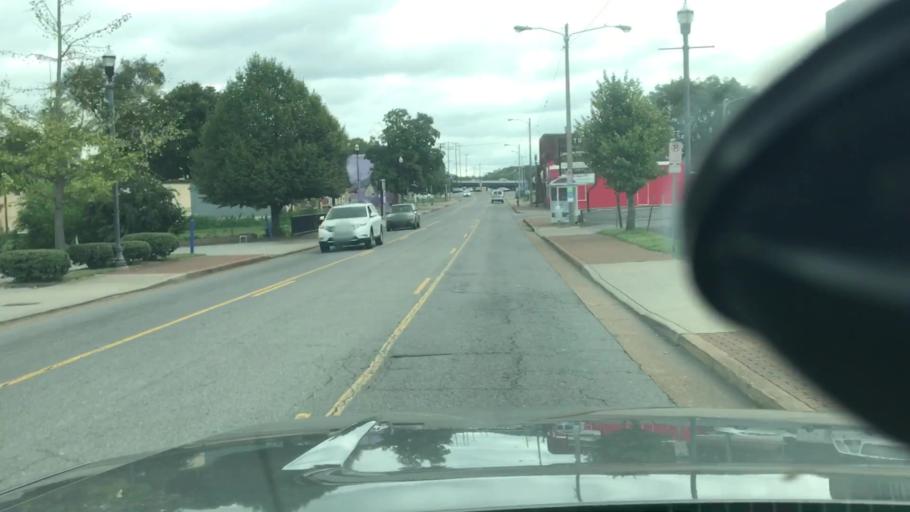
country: US
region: Tennessee
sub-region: Davidson County
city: Nashville
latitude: 36.1678
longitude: -86.8195
